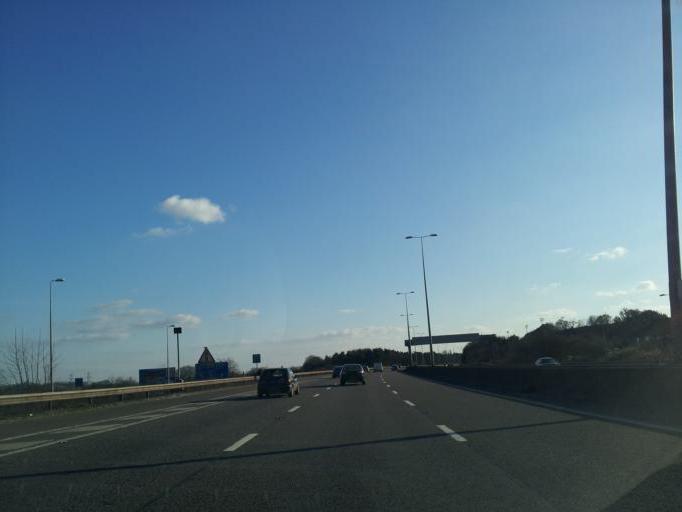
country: GB
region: England
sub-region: Devon
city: Topsham
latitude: 50.7155
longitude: -3.4623
